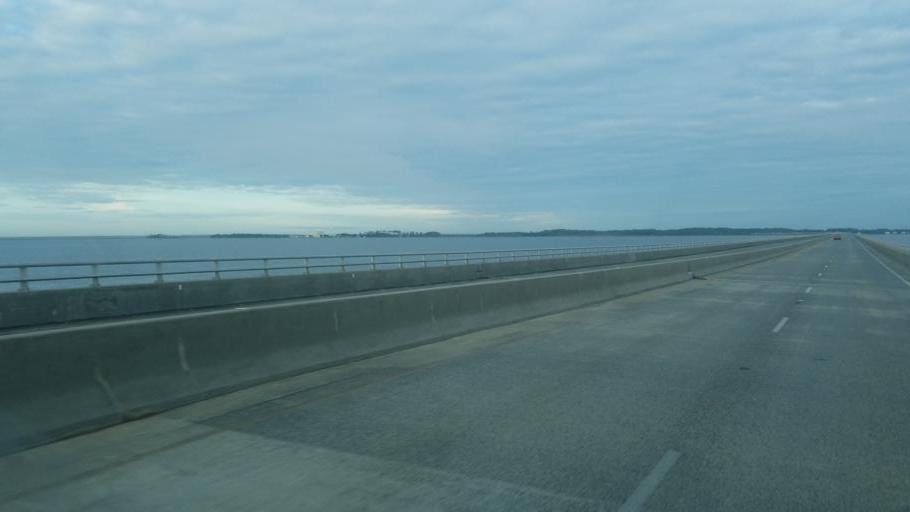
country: US
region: North Carolina
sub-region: Dare County
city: Manteo
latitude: 35.8863
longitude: -75.7254
